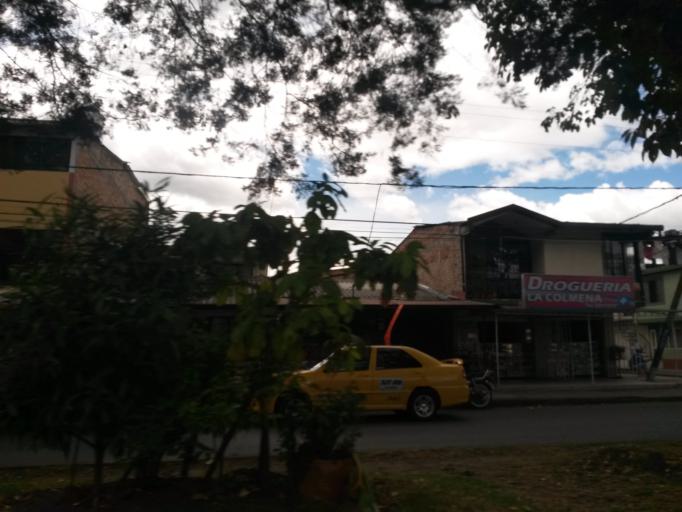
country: CO
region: Cauca
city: Popayan
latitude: 2.4364
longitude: -76.6143
